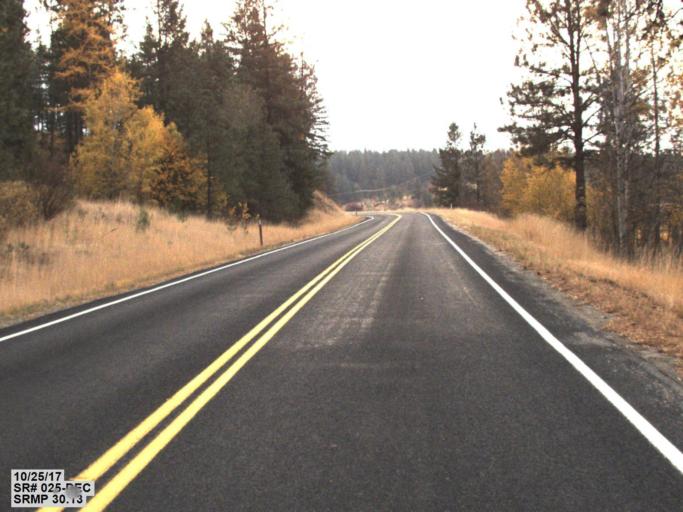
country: US
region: Washington
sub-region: Lincoln County
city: Davenport
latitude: 47.9840
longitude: -118.2915
